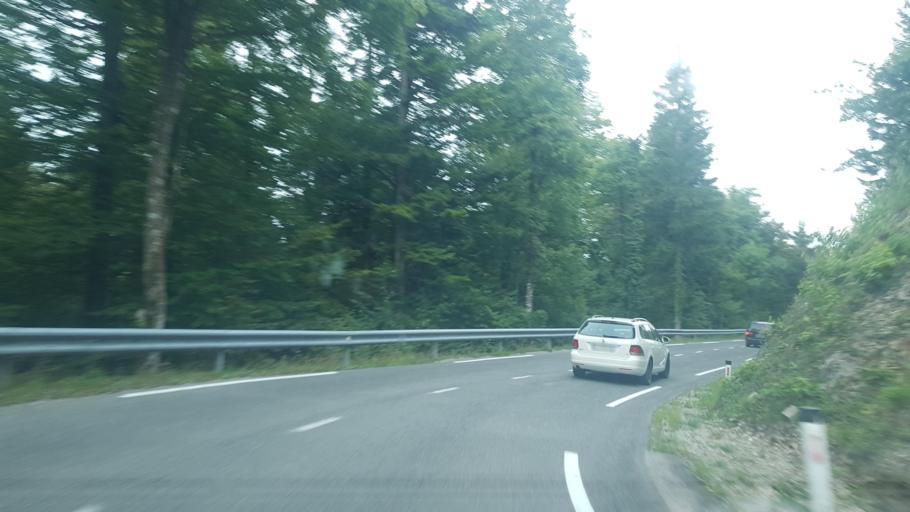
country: SI
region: Logatec
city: Logatec
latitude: 45.8914
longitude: 14.1604
